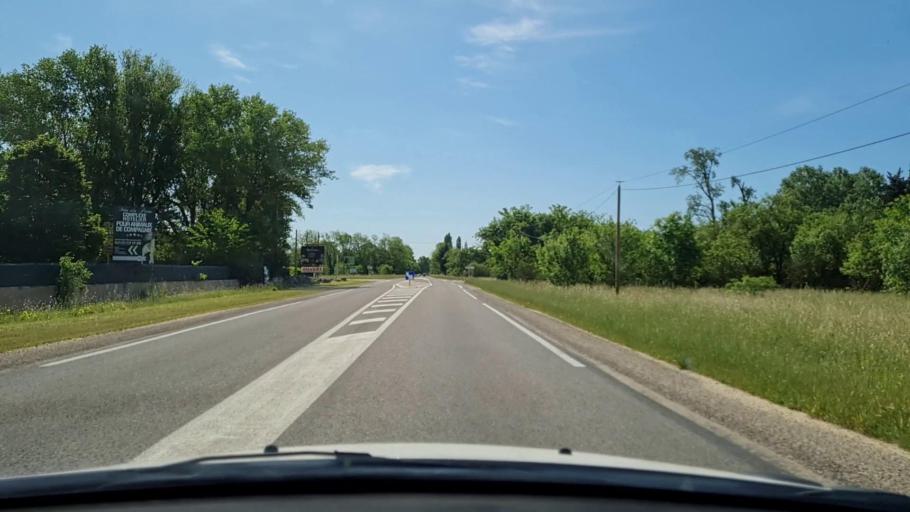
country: FR
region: Languedoc-Roussillon
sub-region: Departement du Gard
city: Saint-Genies-de-Malgoires
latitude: 43.9578
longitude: 4.2403
